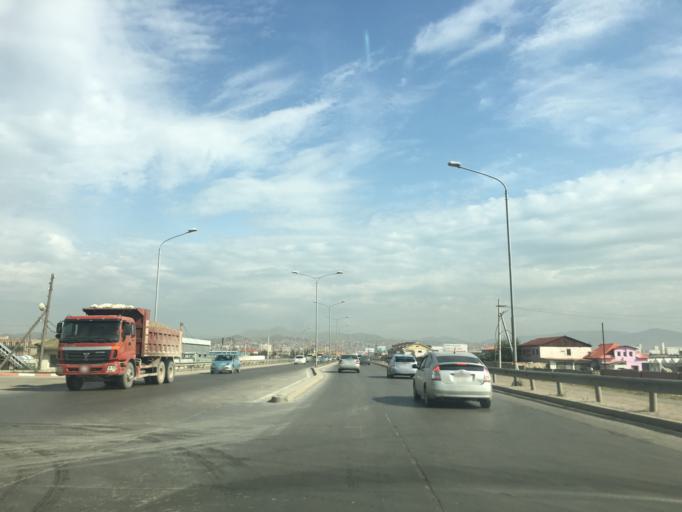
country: MN
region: Ulaanbaatar
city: Ulaanbaatar
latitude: 47.8942
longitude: 106.7855
